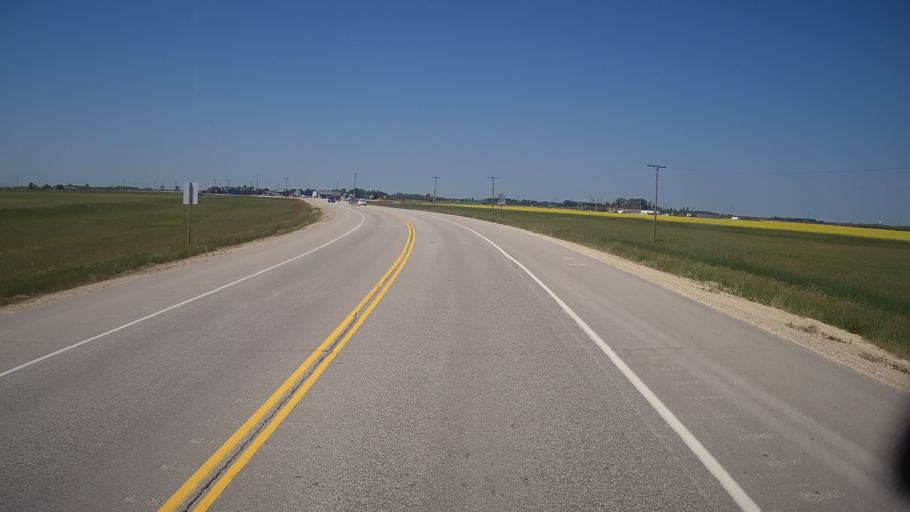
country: CA
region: Manitoba
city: Stonewall
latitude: 49.9890
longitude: -97.3138
